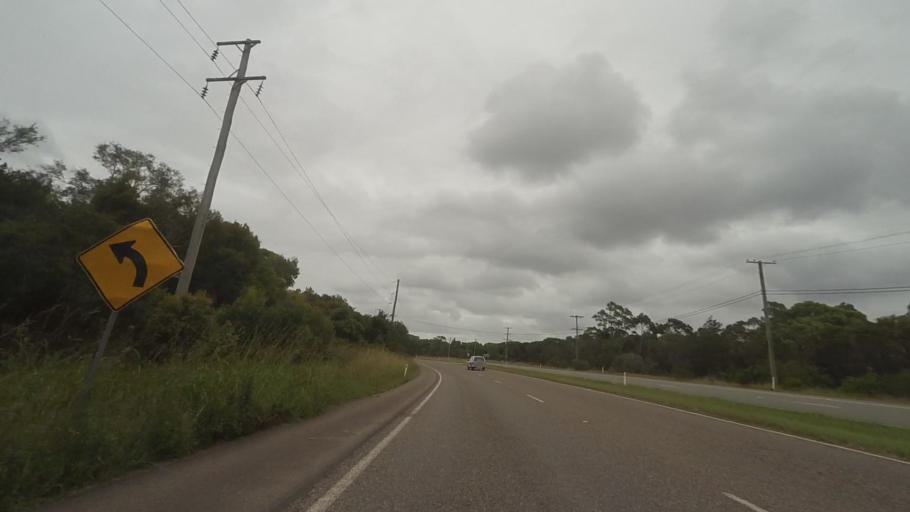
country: AU
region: New South Wales
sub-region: Wyong Shire
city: Kingfisher Shores
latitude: -33.1891
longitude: 151.5295
